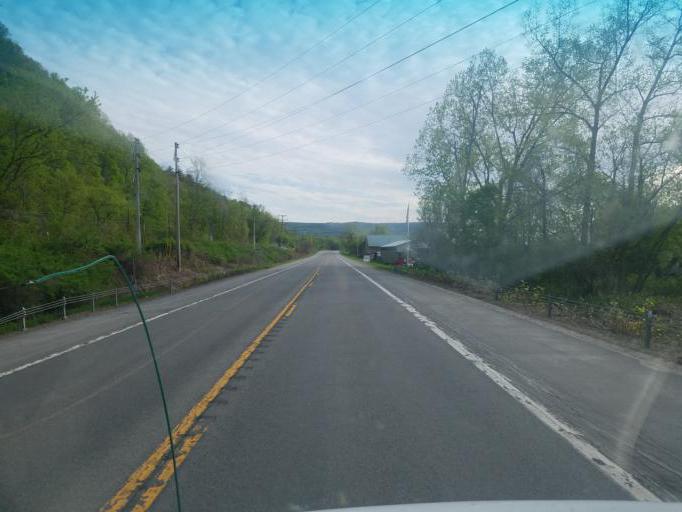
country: US
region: New York
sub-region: Herkimer County
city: Little Falls
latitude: 43.0356
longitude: -74.8629
